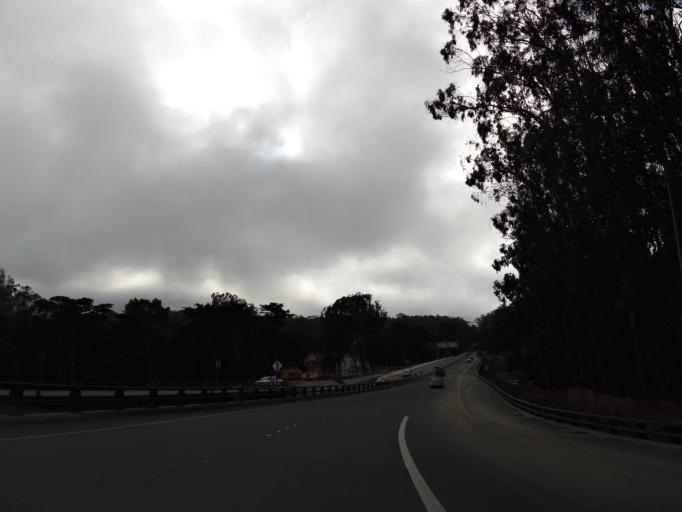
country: US
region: California
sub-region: San Francisco County
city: San Francisco
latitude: 37.8025
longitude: -122.4696
